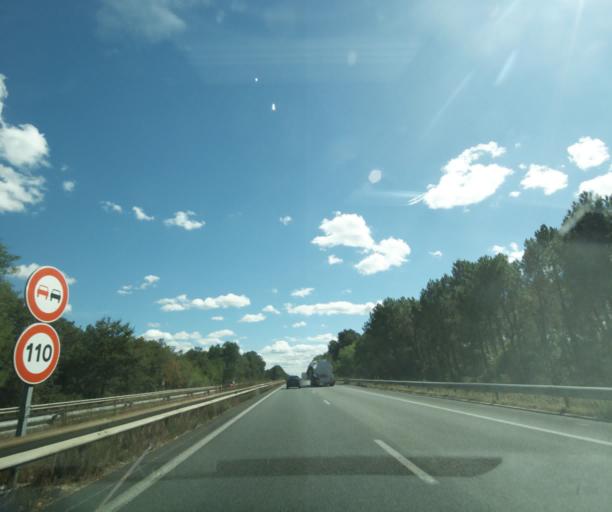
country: FR
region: Aquitaine
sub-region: Departement de la Gironde
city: Saint-Selve
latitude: 44.6687
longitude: -0.4693
